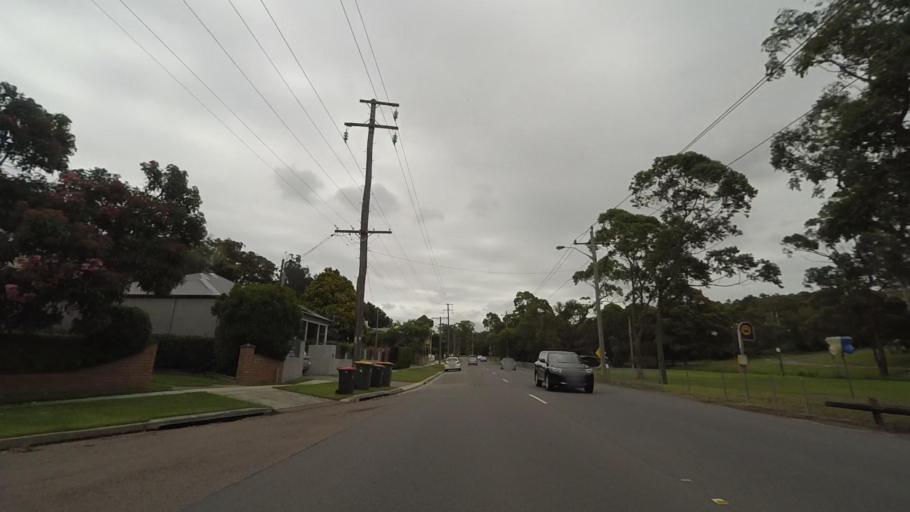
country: AU
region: New South Wales
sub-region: Lake Macquarie Shire
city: Kotara
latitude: -32.9426
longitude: 151.6986
